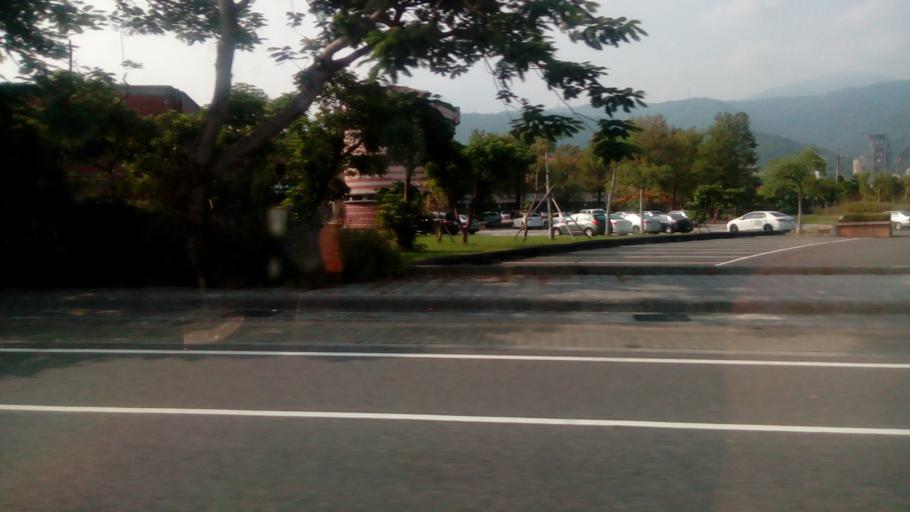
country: TW
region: Taiwan
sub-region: Yilan
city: Yilan
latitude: 24.6329
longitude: 121.7920
